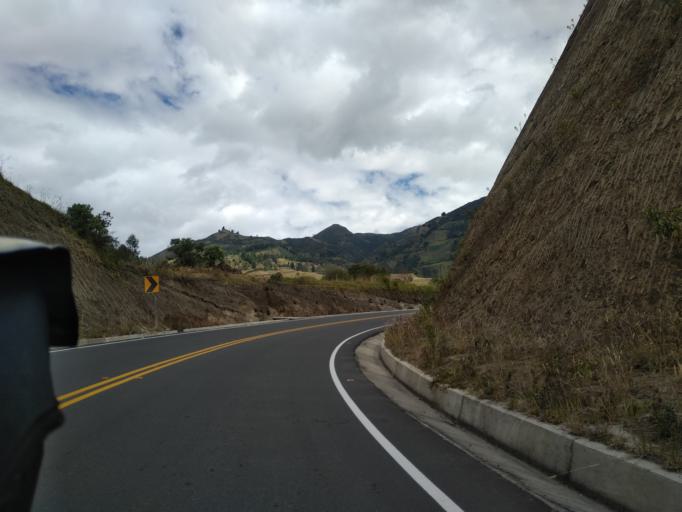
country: EC
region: Cotopaxi
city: Saquisili
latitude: -0.7261
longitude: -78.8916
